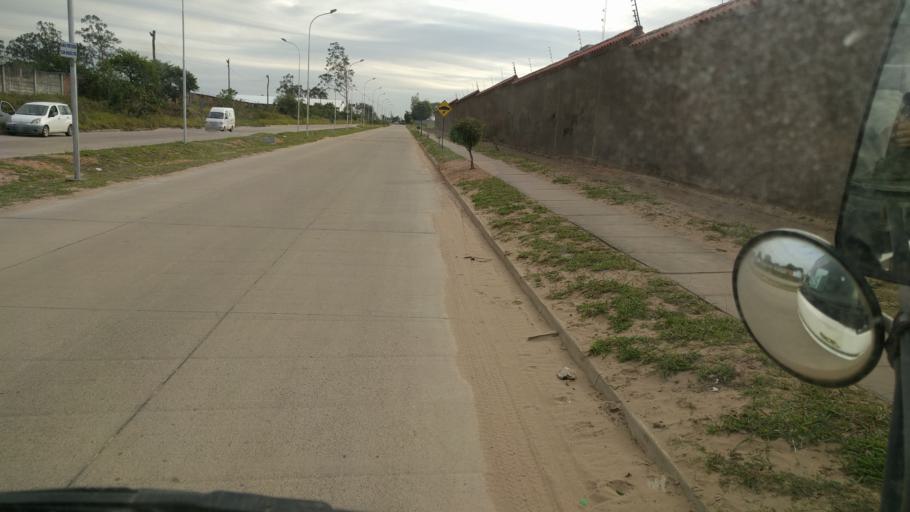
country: BO
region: Santa Cruz
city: Santa Cruz de la Sierra
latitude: -17.6832
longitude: -63.1546
